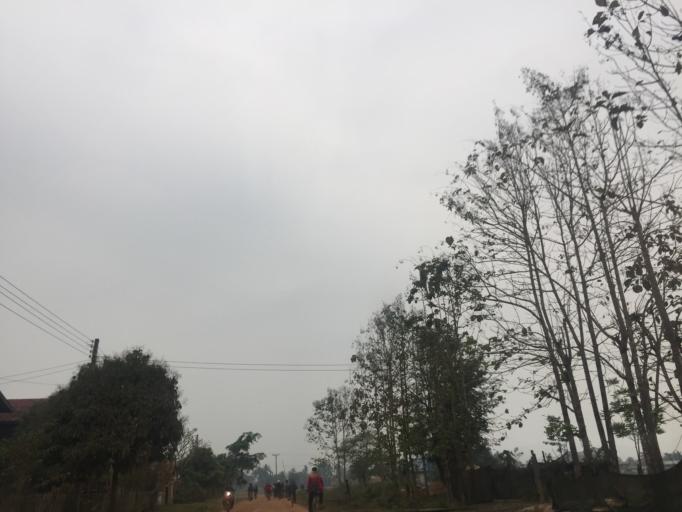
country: LA
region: Xiagnabouli
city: Sainyabuli
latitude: 19.0059
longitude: 101.5098
